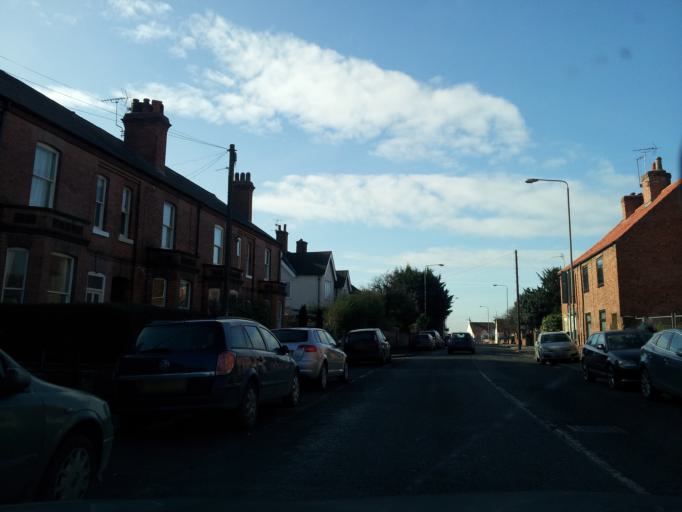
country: GB
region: England
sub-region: Nottinghamshire
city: Newark on Trent
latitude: 53.0721
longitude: -0.8162
